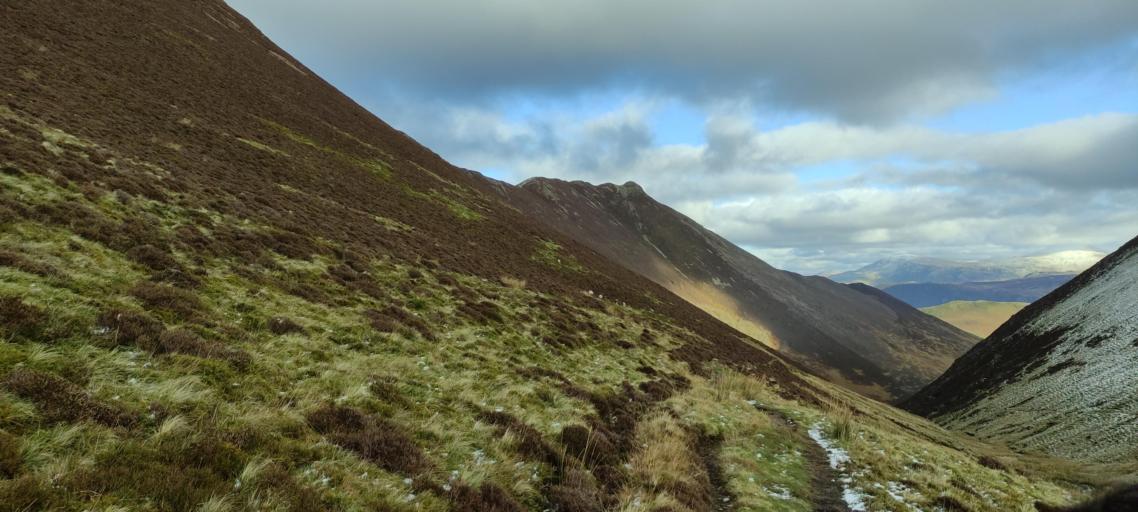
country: GB
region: England
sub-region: Cumbria
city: Keswick
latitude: 54.5701
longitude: -3.2308
